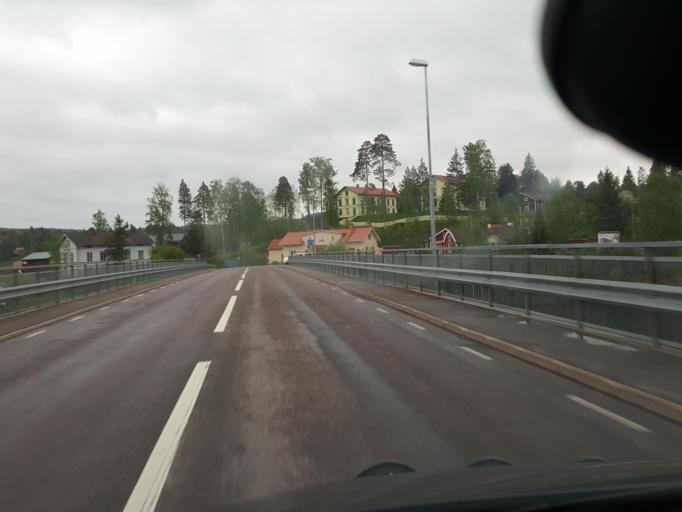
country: SE
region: Gaevleborg
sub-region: Ljusdals Kommun
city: Jaervsoe
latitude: 61.7111
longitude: 16.1840
